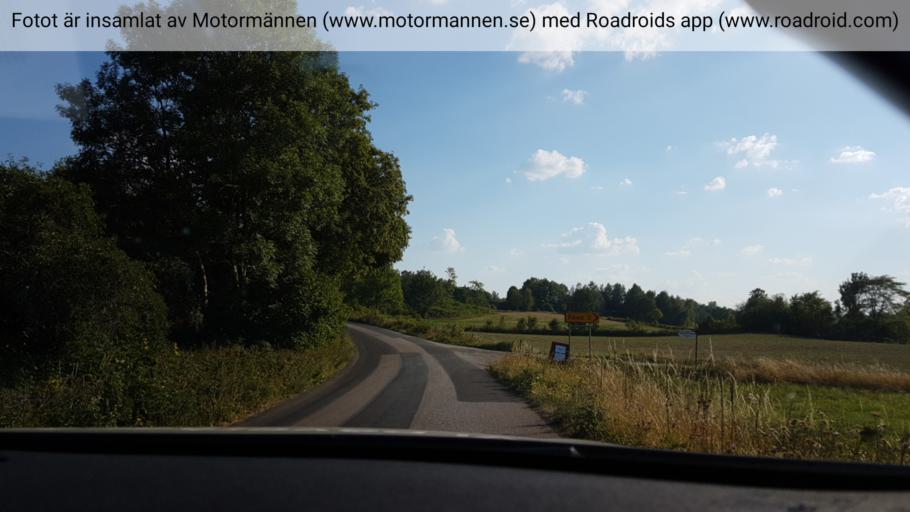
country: SE
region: Vaestra Goetaland
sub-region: Skovde Kommun
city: Skoevde
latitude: 58.4481
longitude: 13.7089
